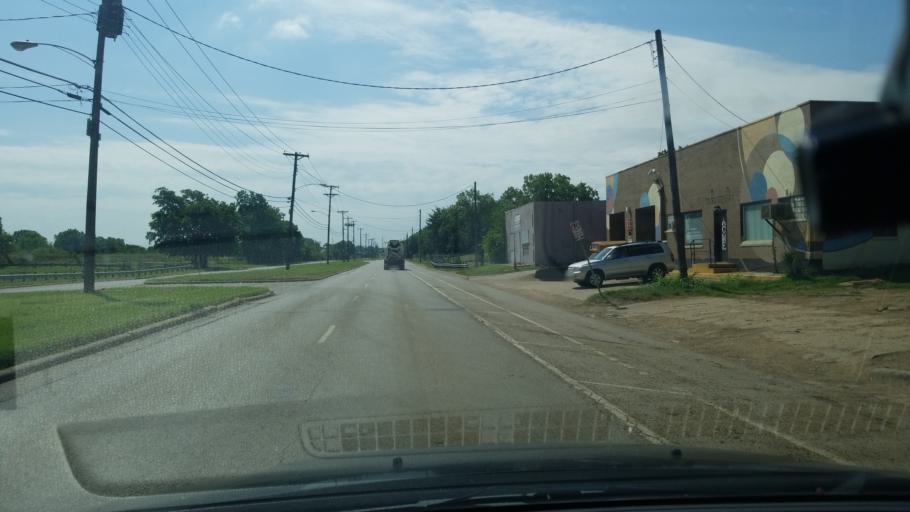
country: US
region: Texas
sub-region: Dallas County
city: Dallas
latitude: 32.7638
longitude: -96.8011
